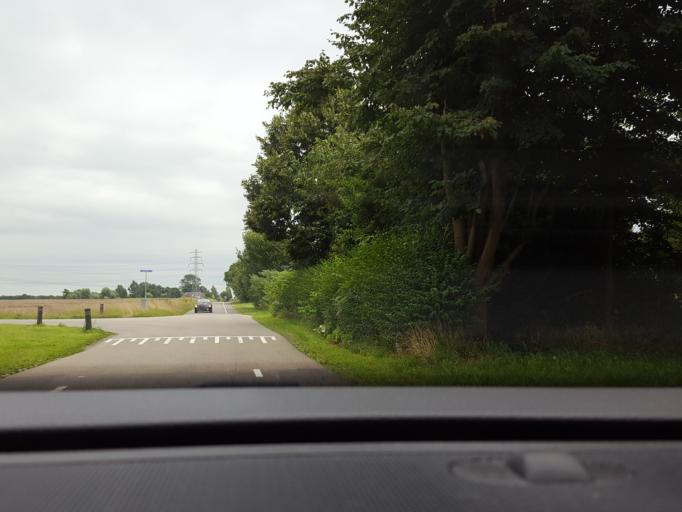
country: NL
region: Gelderland
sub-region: Gemeente Zutphen
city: Leesten
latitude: 52.1153
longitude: 6.2236
